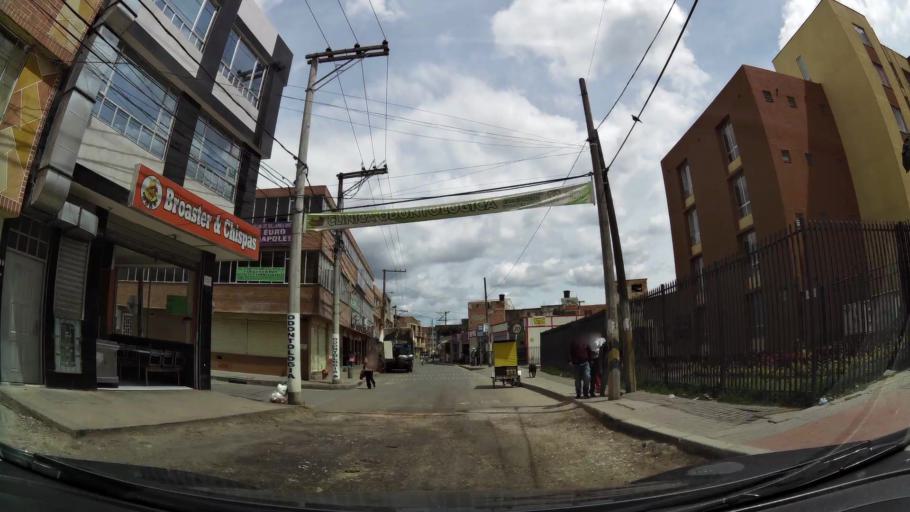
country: CO
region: Cundinamarca
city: Funza
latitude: 4.7150
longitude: -74.1352
